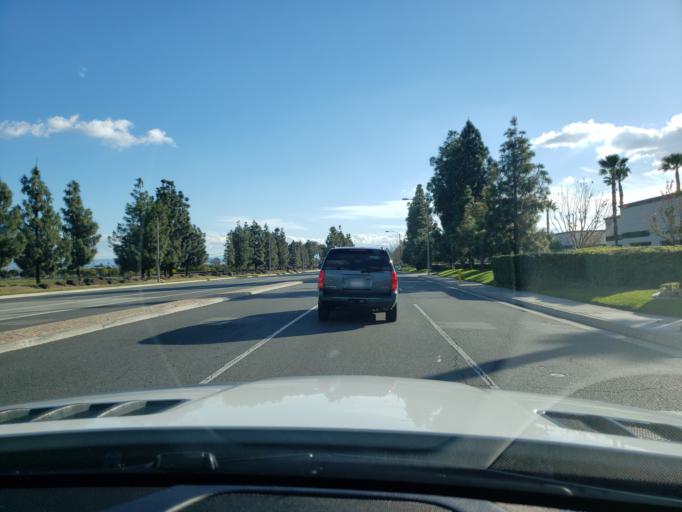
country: US
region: California
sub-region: San Bernardino County
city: Rancho Cucamonga
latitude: 34.0480
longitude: -117.5584
